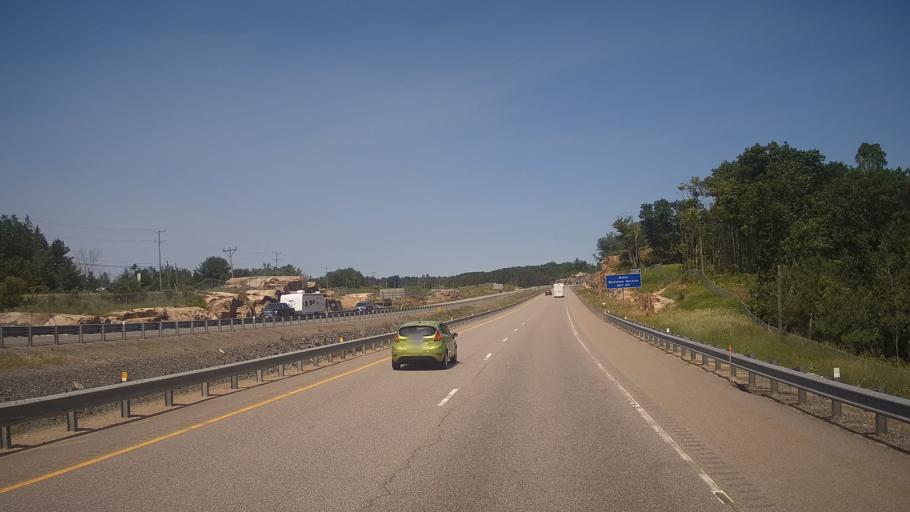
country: CA
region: Ontario
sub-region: Parry Sound District
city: Parry Sound
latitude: 45.3959
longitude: -80.0573
